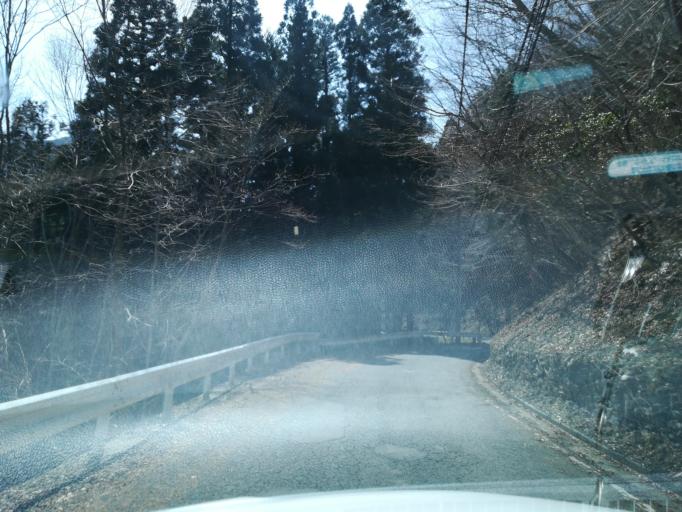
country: JP
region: Tokushima
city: Wakimachi
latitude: 33.8558
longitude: 134.0480
